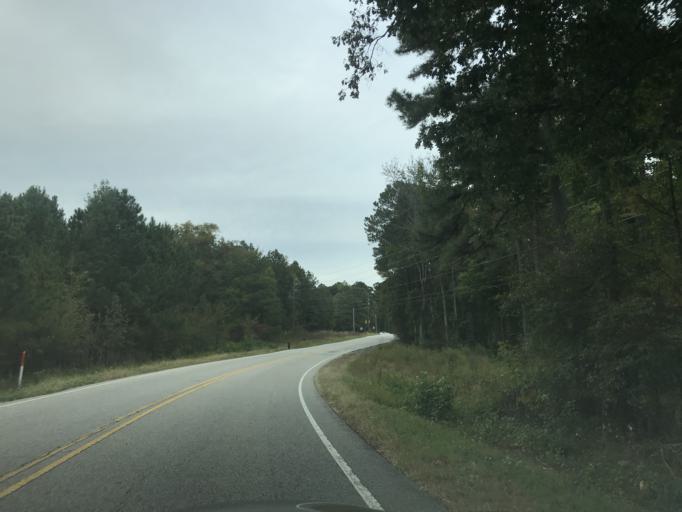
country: US
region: North Carolina
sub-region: Wake County
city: Knightdale
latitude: 35.8429
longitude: -78.5153
